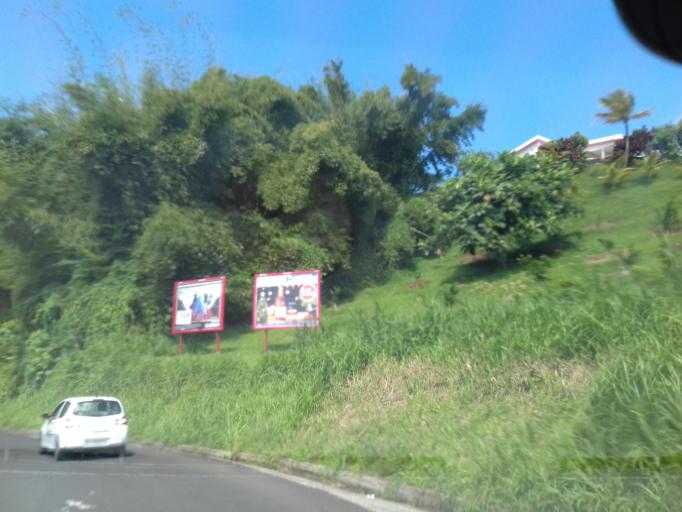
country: MQ
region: Martinique
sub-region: Martinique
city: Saint-Joseph
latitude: 14.6737
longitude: -61.0433
